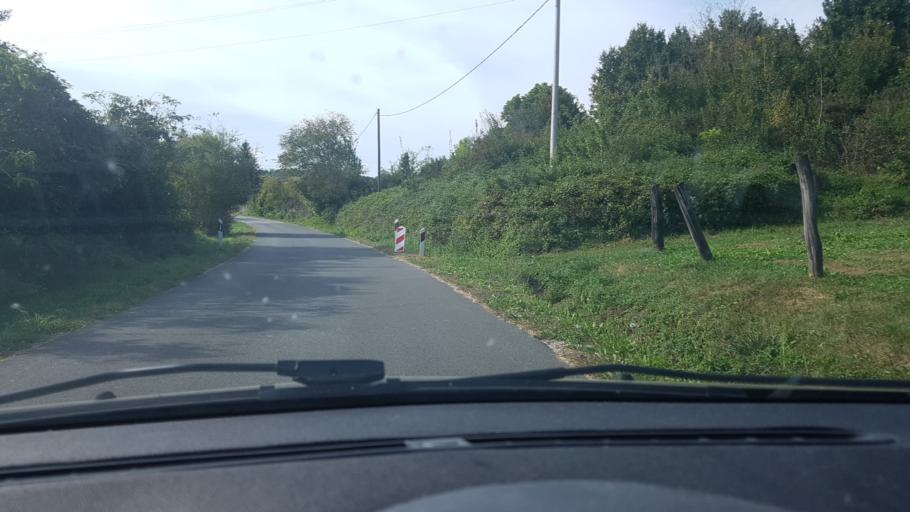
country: HR
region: Krapinsko-Zagorska
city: Zlatar
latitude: 46.1013
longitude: 16.1271
